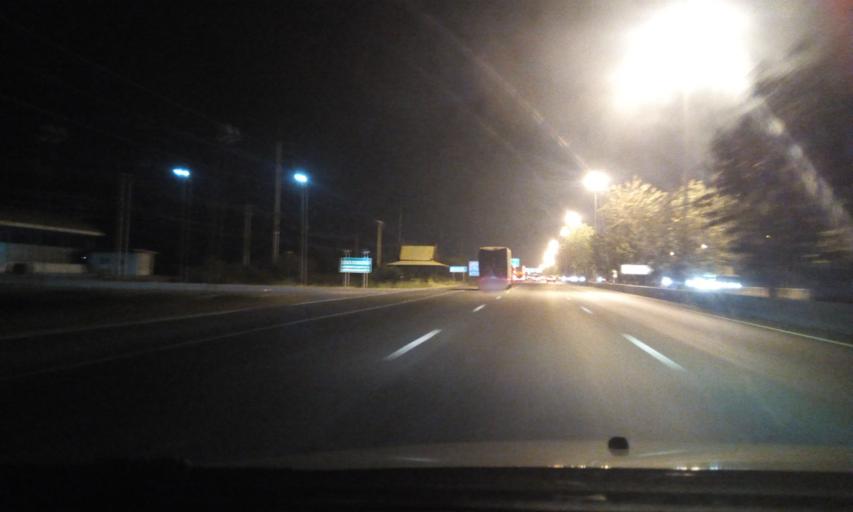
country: TH
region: Ang Thong
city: Chaiyo
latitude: 14.7249
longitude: 100.4553
